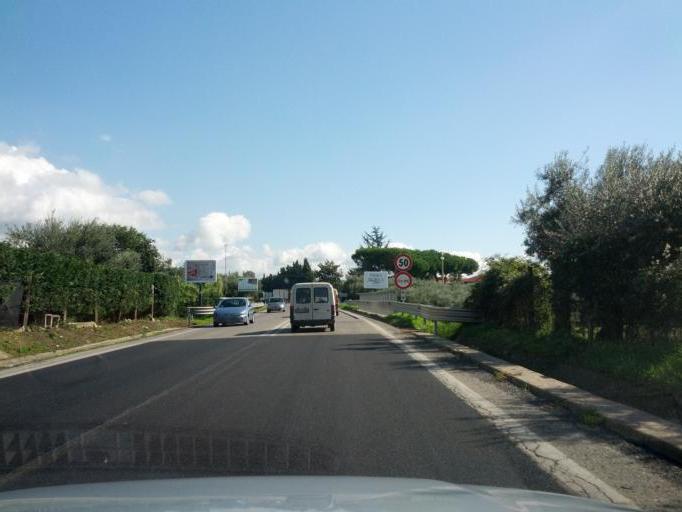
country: IT
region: Latium
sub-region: Provincia di Latina
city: Formia
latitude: 41.2656
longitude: 13.6515
